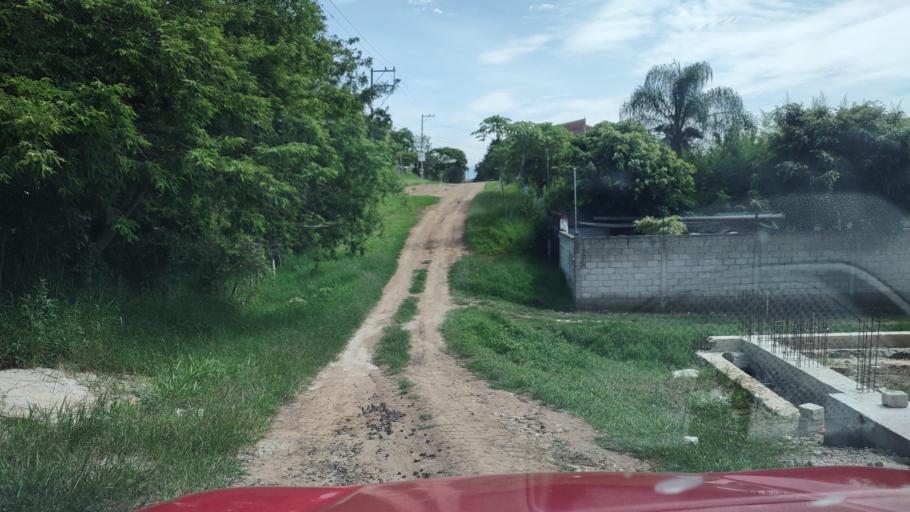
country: MX
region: Veracruz
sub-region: Emiliano Zapata
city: Dos Rios
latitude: 19.4694
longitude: -96.8272
